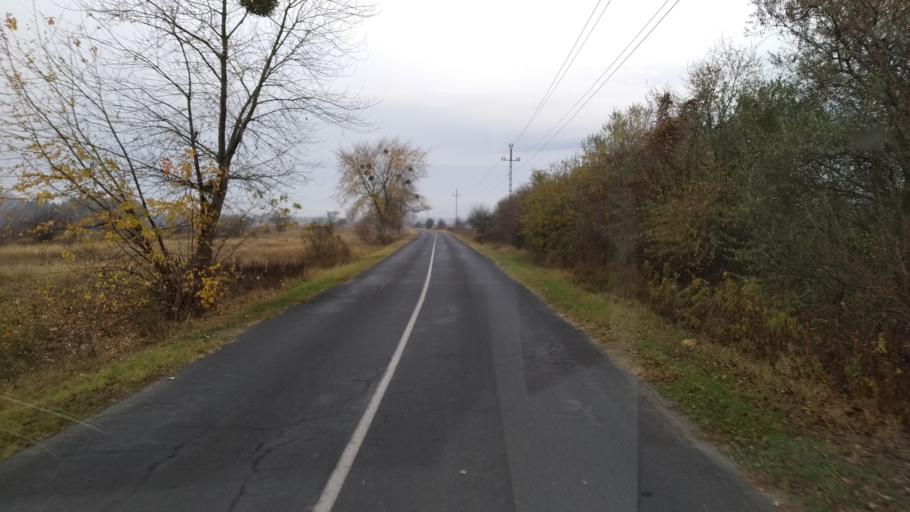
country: HU
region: Pest
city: Tahitotfalu
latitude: 47.7830
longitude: 19.0930
